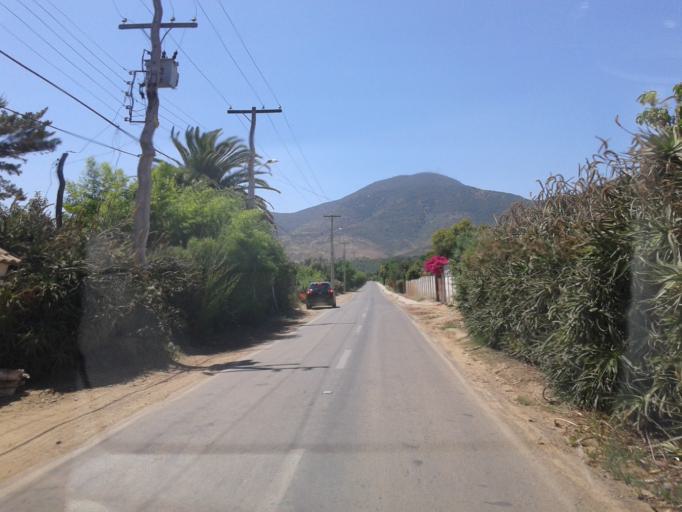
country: CL
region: Valparaiso
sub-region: Provincia de Quillota
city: Hacienda La Calera
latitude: -32.8468
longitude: -71.1905
